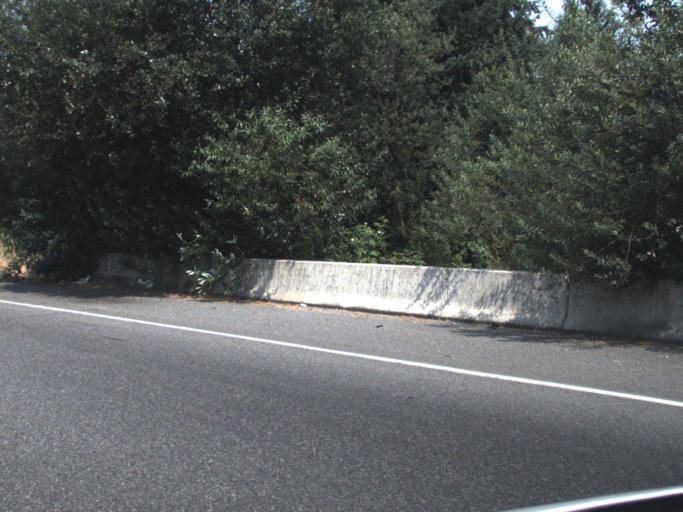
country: US
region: Washington
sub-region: King County
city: Issaquah
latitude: 47.5515
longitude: -122.0683
